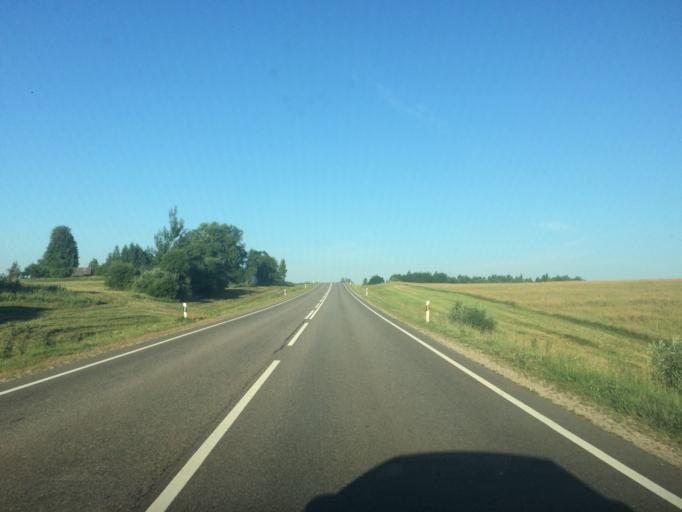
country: LT
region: Utenos apskritis
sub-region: Anyksciai
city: Anyksciai
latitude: 55.3860
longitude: 25.0516
